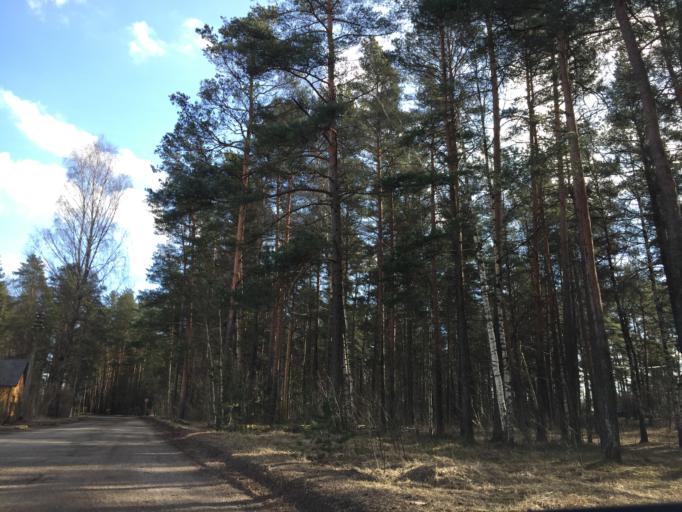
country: LV
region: Incukalns
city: Incukalns
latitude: 57.0959
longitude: 24.6771
